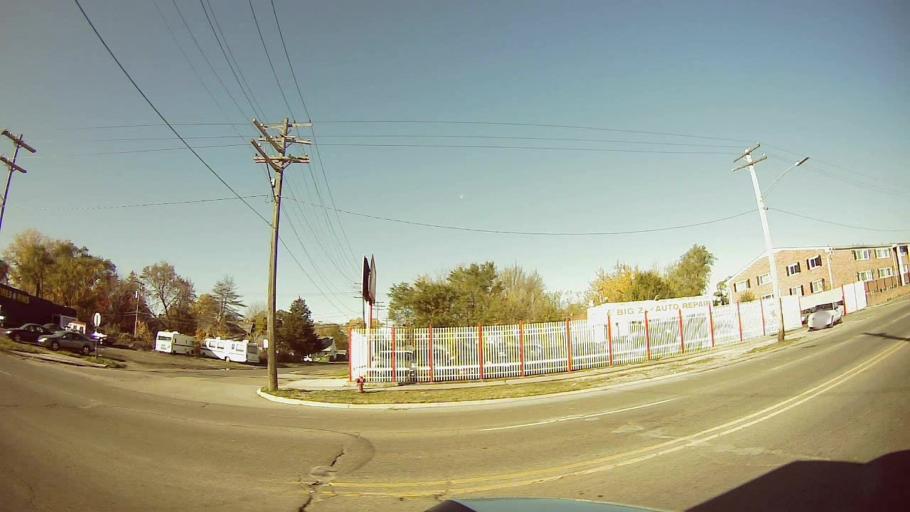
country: US
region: Michigan
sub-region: Wayne County
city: Dearborn
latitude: 42.3704
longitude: -83.1974
